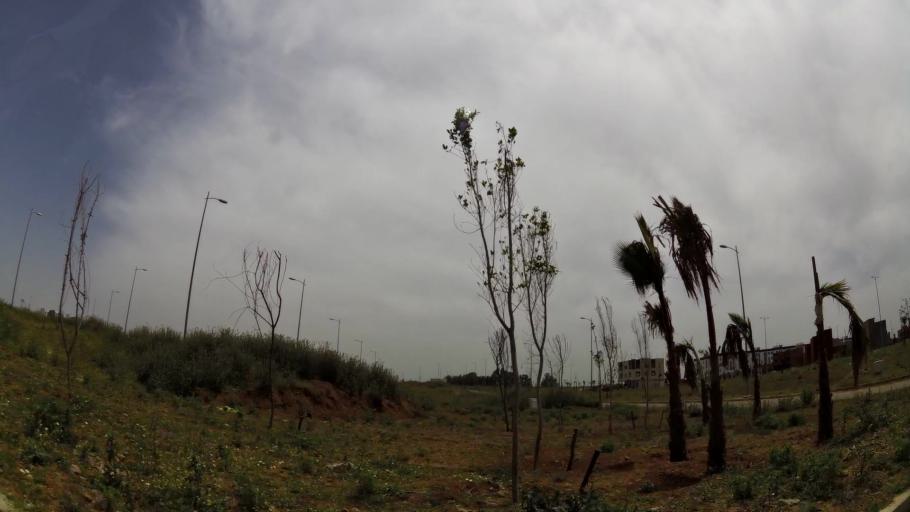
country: MA
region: Rabat-Sale-Zemmour-Zaer
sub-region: Khemisset
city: Khemisset
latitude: 33.8180
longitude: -6.0889
